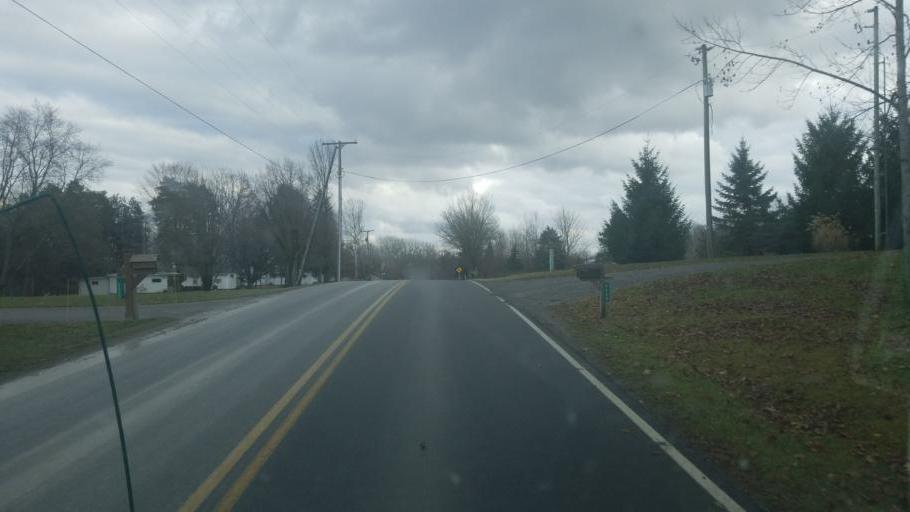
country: US
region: Ohio
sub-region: Wyandot County
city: Upper Sandusky
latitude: 40.7819
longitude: -83.2392
